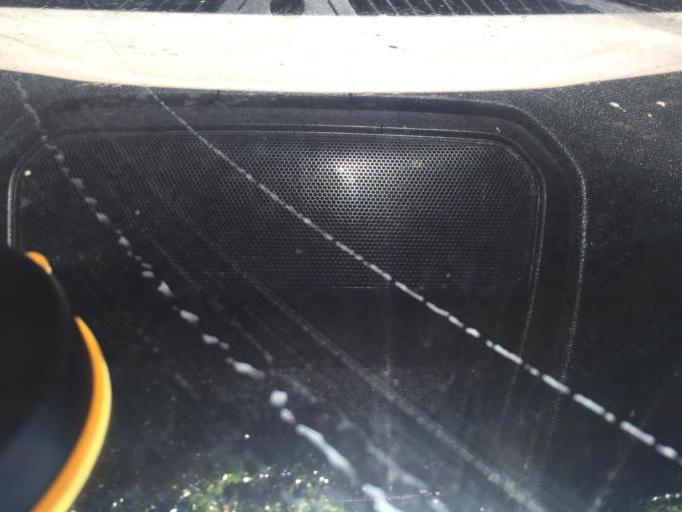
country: LA
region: Phongsali
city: Phongsali
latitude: 21.6557
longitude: 102.4146
